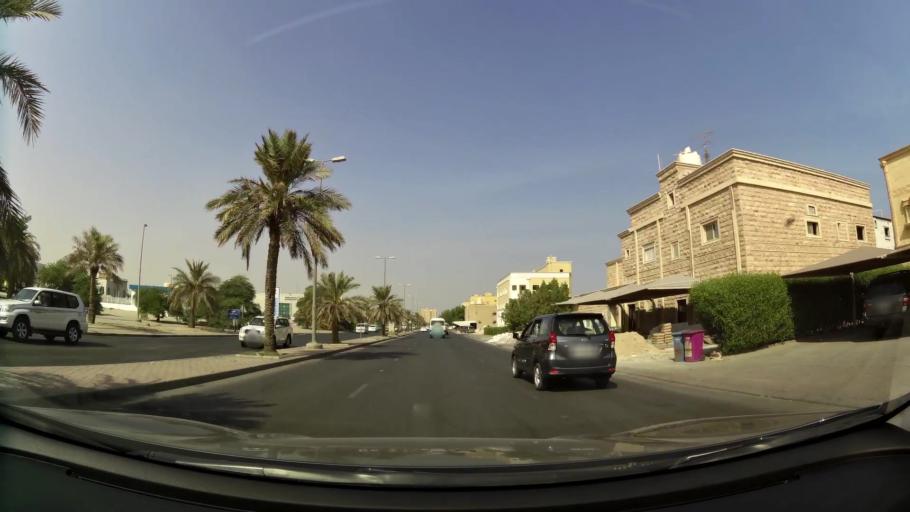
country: KW
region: Al Ahmadi
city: Al Fahahil
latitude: 29.0872
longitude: 48.1227
